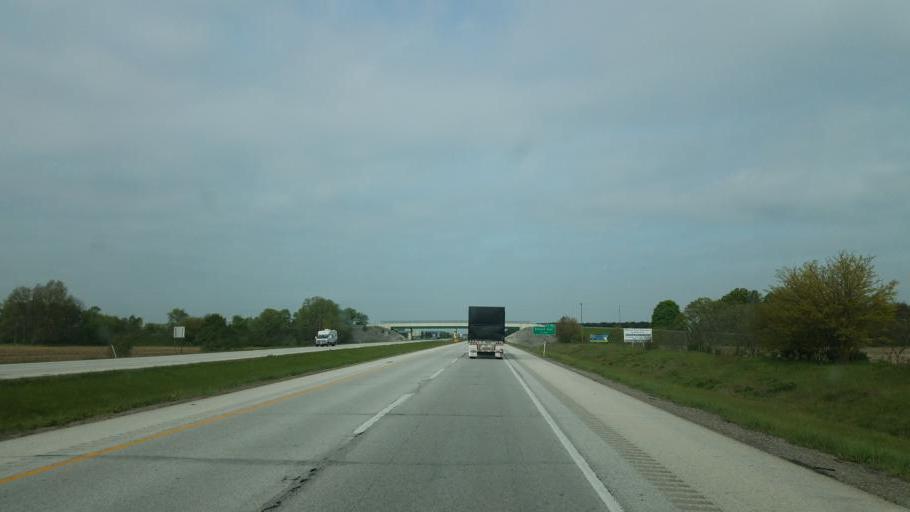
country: US
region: Indiana
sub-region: Elkhart County
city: Bristol
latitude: 41.7312
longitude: -85.8669
